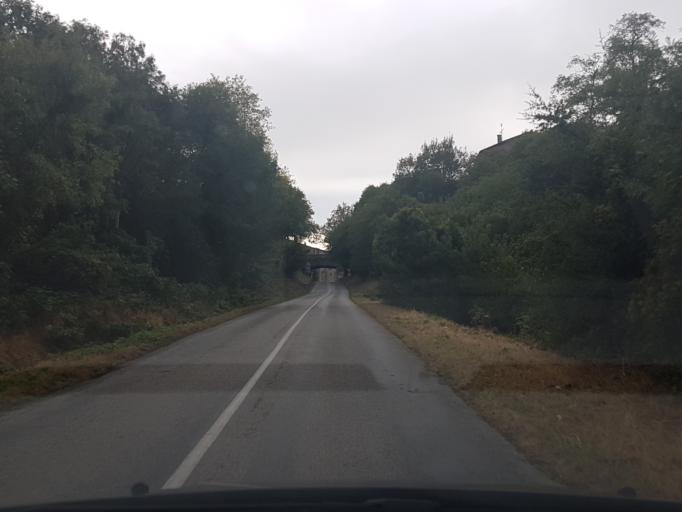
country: FR
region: Languedoc-Roussillon
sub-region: Departement de l'Aude
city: Bram
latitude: 43.1857
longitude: 2.0370
